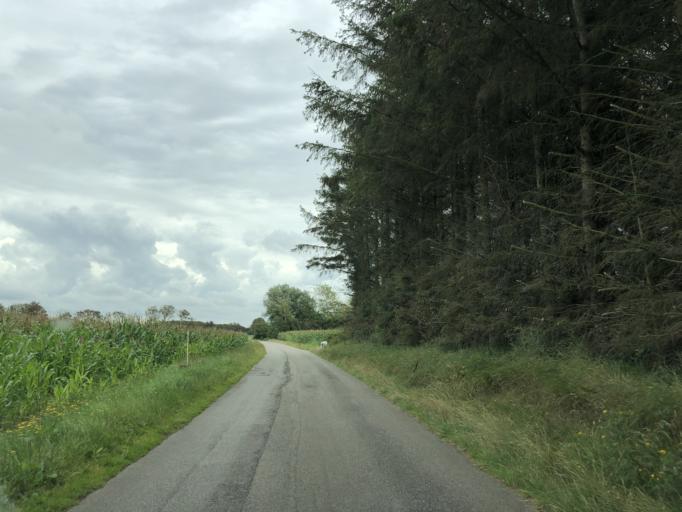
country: DK
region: Central Jutland
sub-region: Ringkobing-Skjern Kommune
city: Ringkobing
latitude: 56.1303
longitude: 8.2649
